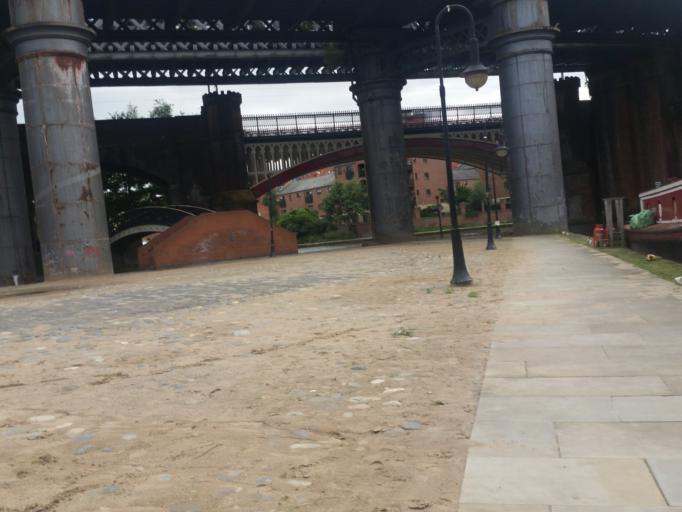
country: GB
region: England
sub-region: Manchester
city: Hulme
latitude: 53.4755
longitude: -2.2569
